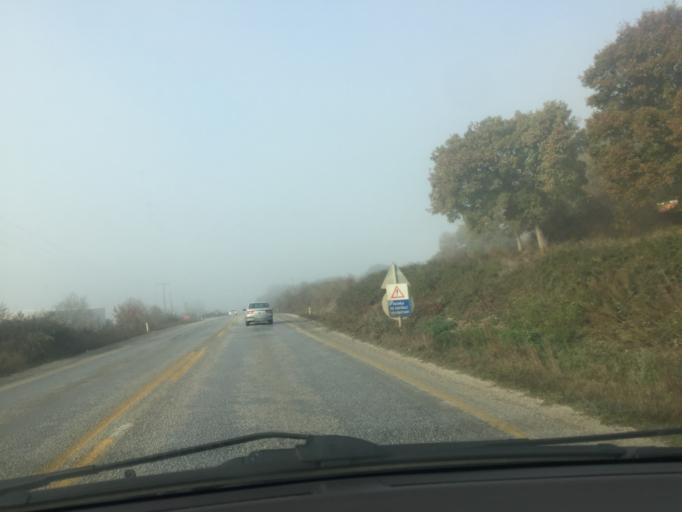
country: TR
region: Canakkale
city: Can
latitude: 40.0048
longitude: 27.0443
